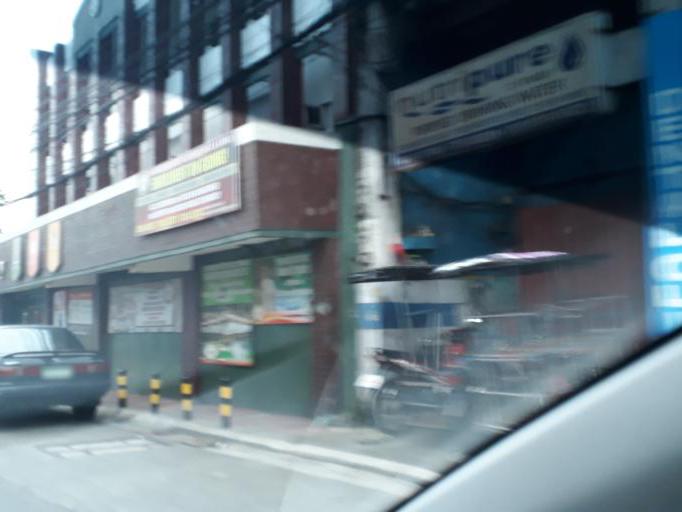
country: PH
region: Metro Manila
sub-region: City of Manila
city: Manila
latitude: 14.6264
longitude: 120.9919
